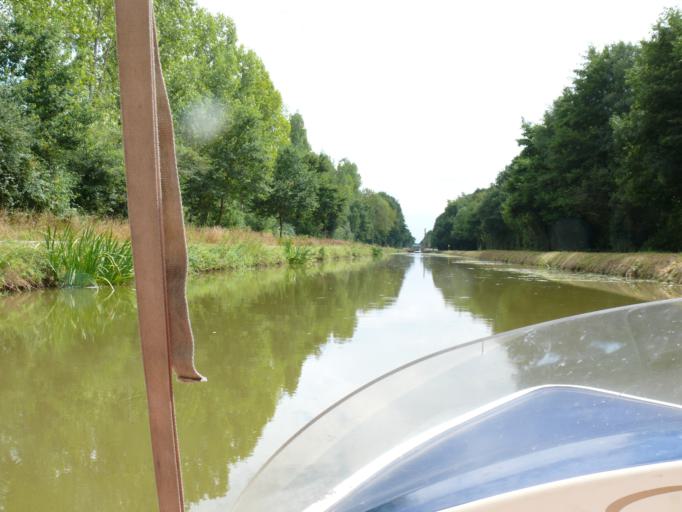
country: FR
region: Auvergne
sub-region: Departement de l'Allier
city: Vallon-en-Sully
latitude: 46.5211
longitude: 2.6157
